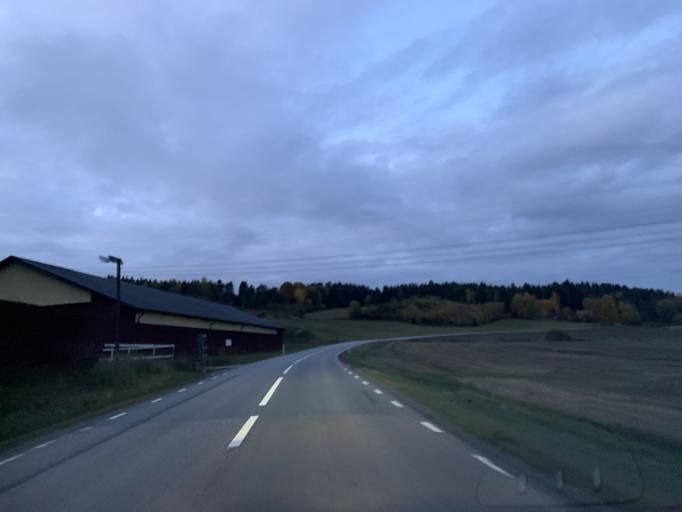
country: SE
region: Stockholm
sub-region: Botkyrka Kommun
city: Varsta
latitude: 59.1192
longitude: 17.8037
